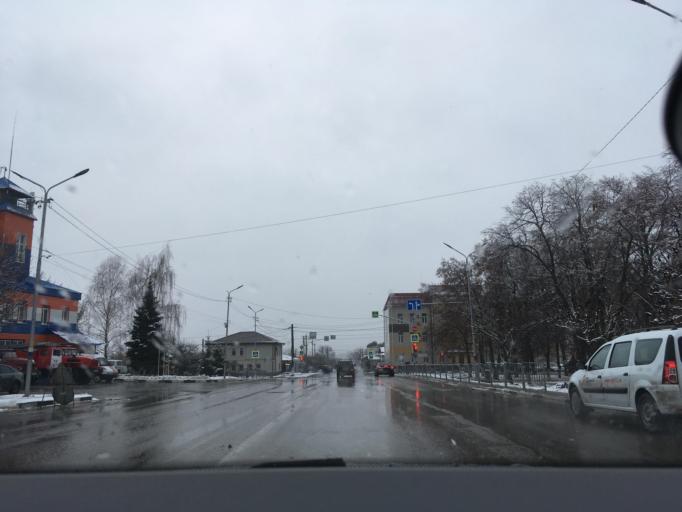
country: RU
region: Belgorod
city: Valuyki
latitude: 50.2101
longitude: 38.1004
